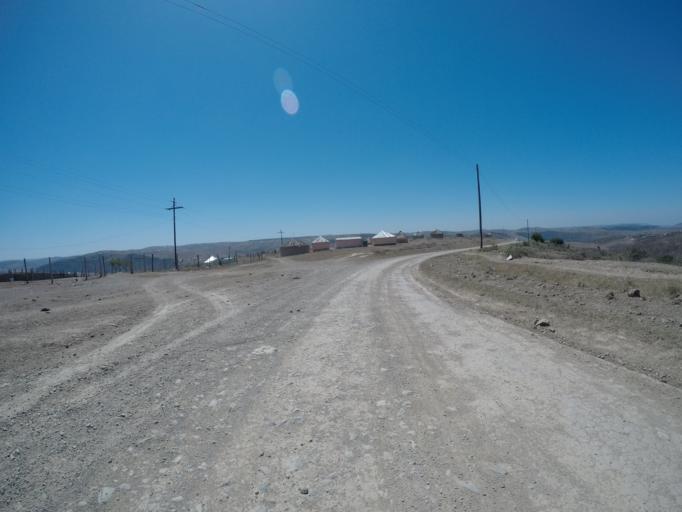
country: ZA
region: Eastern Cape
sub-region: OR Tambo District Municipality
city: Mthatha
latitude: -31.8806
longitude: 28.8749
